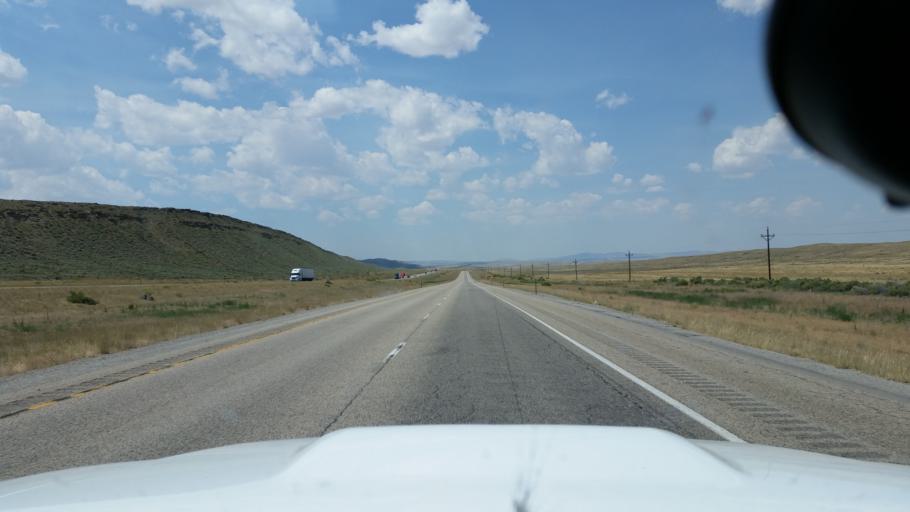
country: US
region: Wyoming
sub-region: Carbon County
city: Saratoga
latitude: 41.7437
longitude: -106.8880
